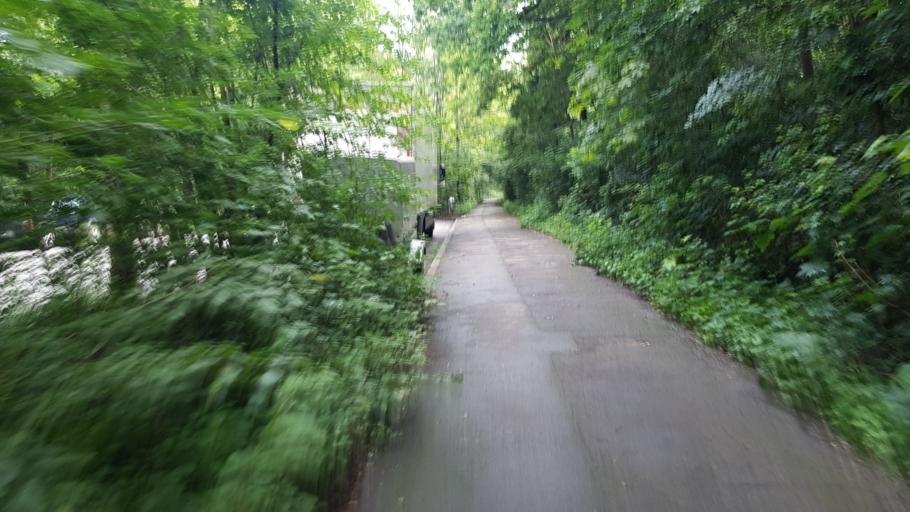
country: DE
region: Bavaria
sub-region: Upper Bavaria
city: Pasing
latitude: 48.1666
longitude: 11.4927
